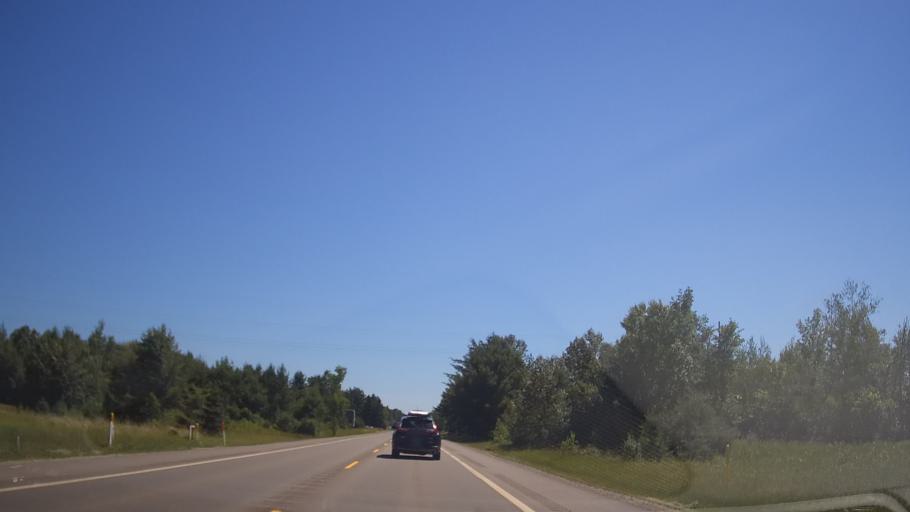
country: US
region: Michigan
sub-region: Cheboygan County
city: Indian River
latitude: 45.6011
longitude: -84.7824
